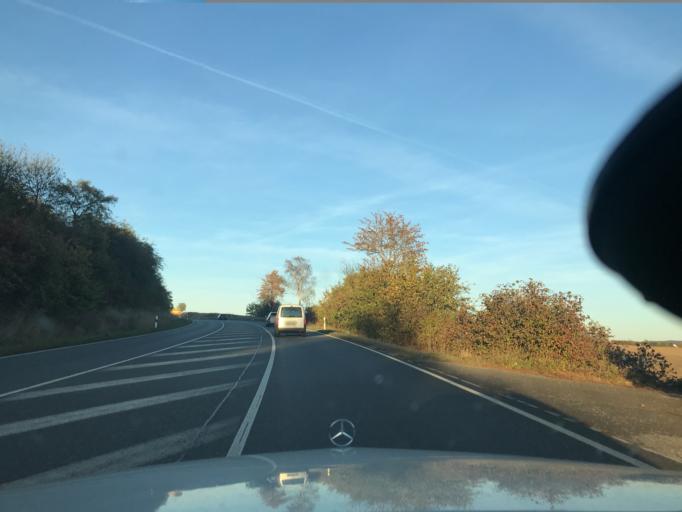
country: DE
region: Hesse
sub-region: Regierungsbezirk Kassel
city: Eschwege
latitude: 51.1739
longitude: 10.0302
